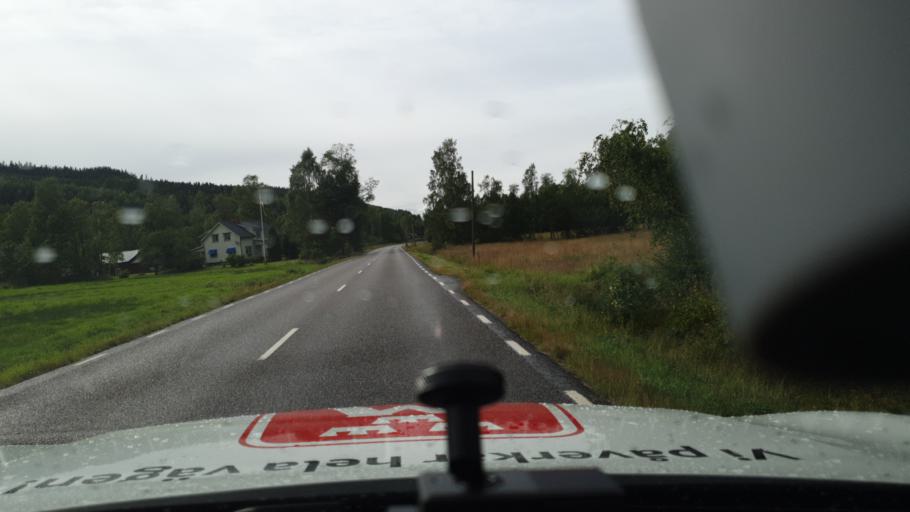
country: SE
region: Vaermland
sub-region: Sunne Kommun
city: Sunne
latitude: 59.8058
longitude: 13.0385
